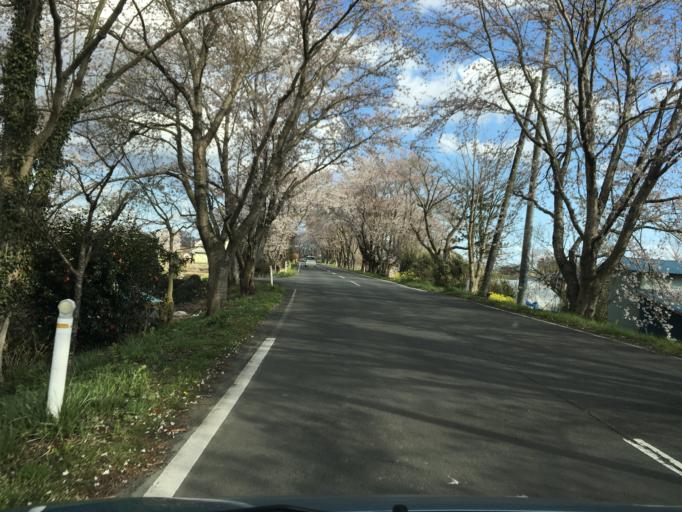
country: JP
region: Miyagi
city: Wakuya
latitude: 38.6452
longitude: 141.1629
